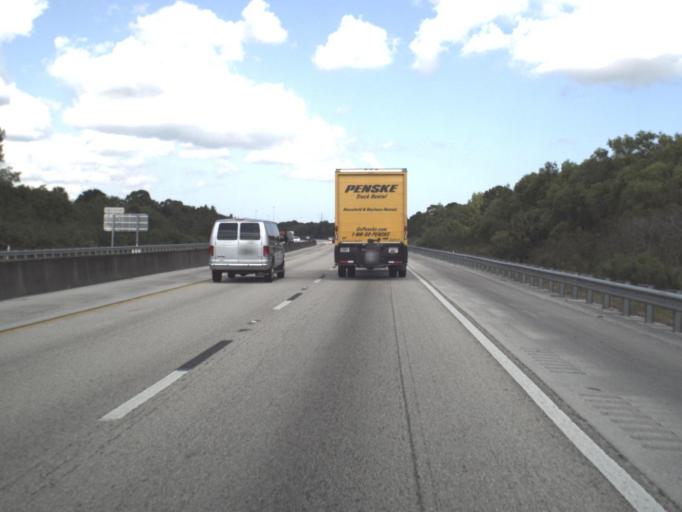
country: US
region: Florida
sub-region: Palm Beach County
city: Palm Beach Gardens
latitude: 26.8713
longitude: -80.1287
